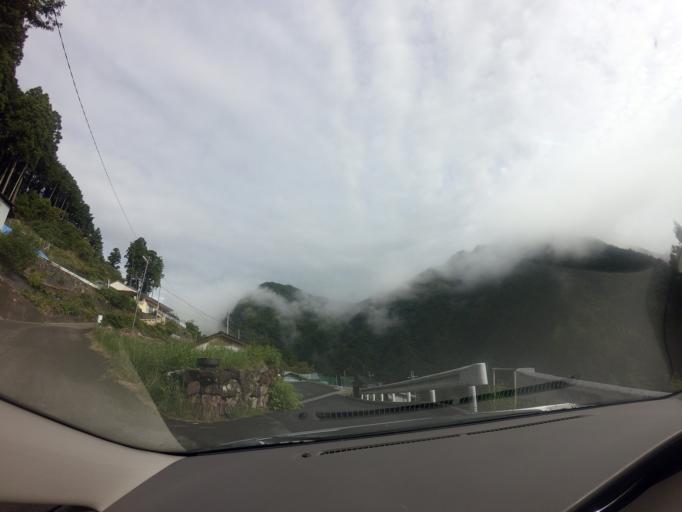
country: JP
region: Wakayama
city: Shingu
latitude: 33.9672
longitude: 135.8123
